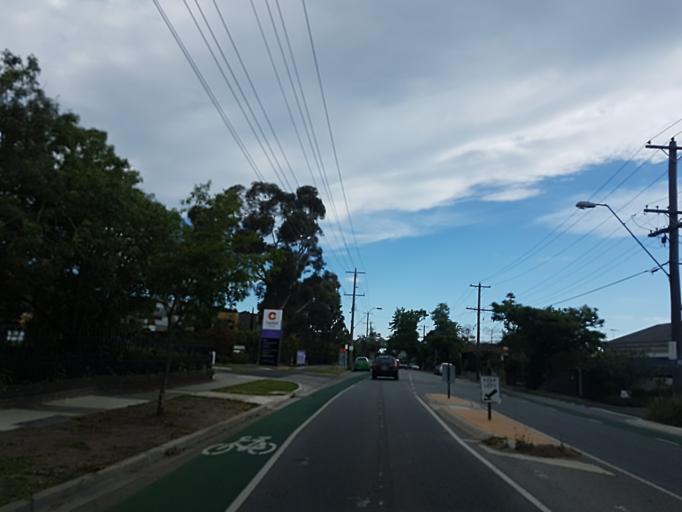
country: AU
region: Victoria
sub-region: Glen Eira
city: Caulfield
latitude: -37.8833
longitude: 145.0155
